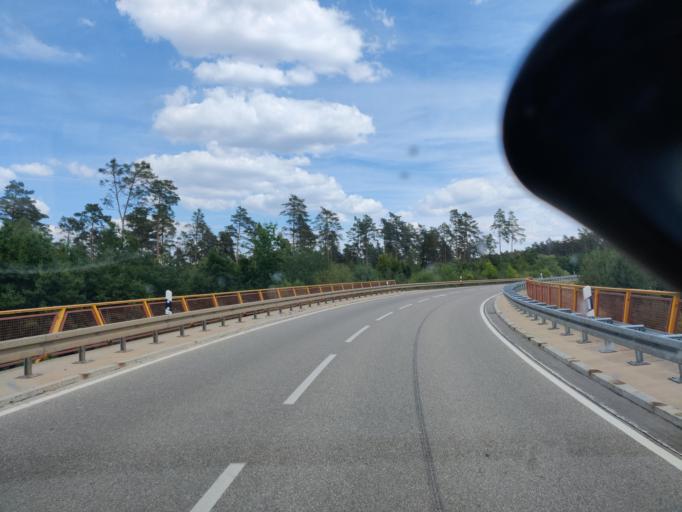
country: DE
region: Bavaria
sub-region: Regierungsbezirk Mittelfranken
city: Rottenbach
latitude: 49.1319
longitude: 11.0268
